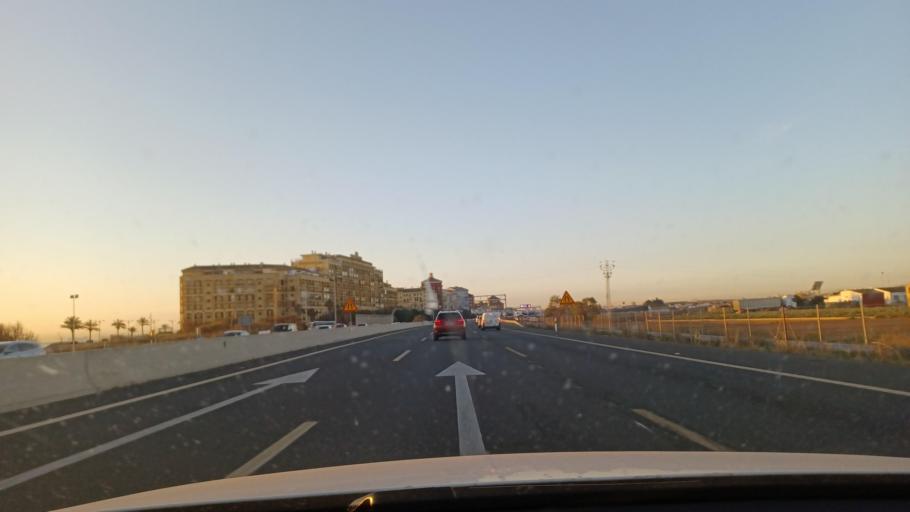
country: ES
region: Valencia
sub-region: Provincia de Valencia
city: Meliana
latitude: 39.5173
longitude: -0.3202
